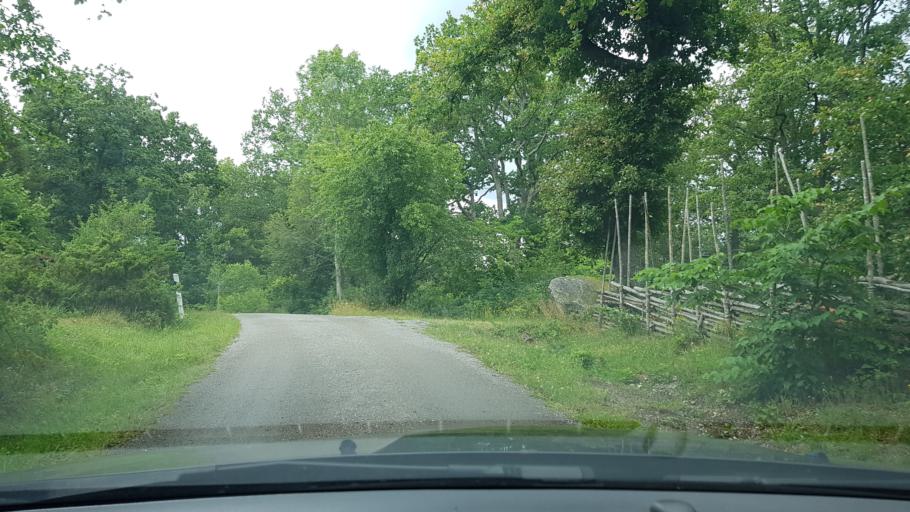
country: SE
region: Uppsala
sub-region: Uppsala Kommun
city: Alsike
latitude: 59.7247
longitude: 17.6888
